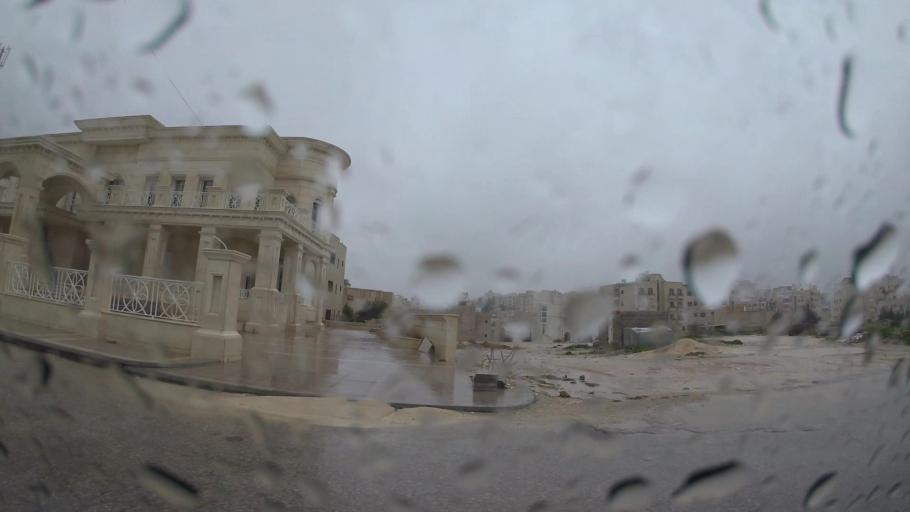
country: JO
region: Amman
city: Al Jubayhah
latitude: 32.0132
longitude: 35.8951
